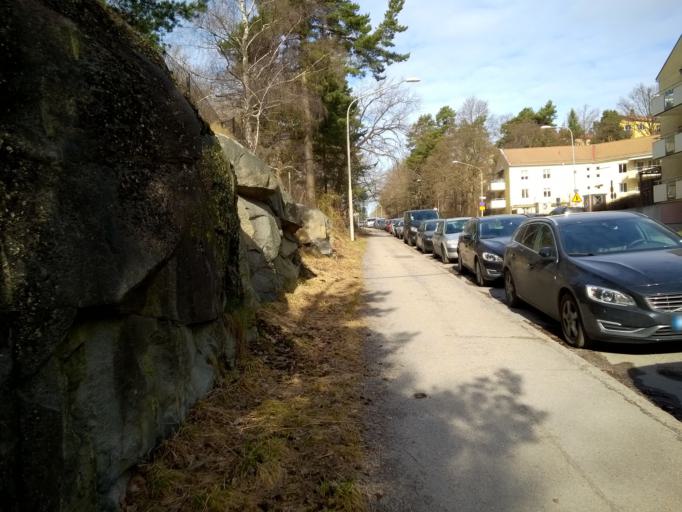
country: SE
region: Stockholm
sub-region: Sundbybergs Kommun
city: Sundbyberg
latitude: 59.3365
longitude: 17.9844
